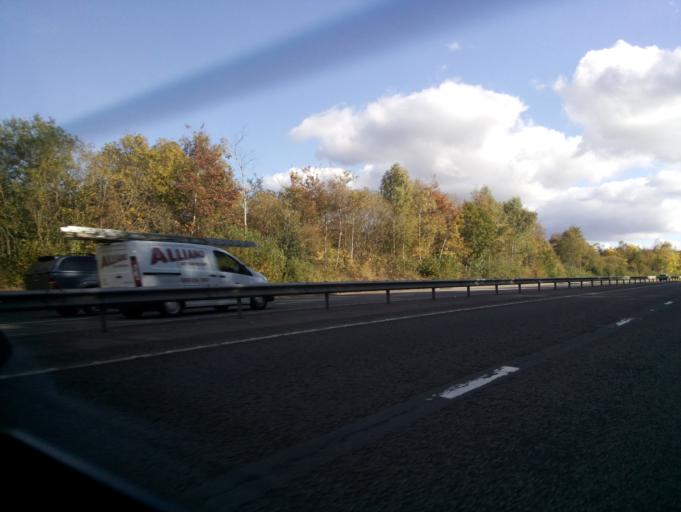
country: GB
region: Wales
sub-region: Merthyr Tydfil County Borough
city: Abercanaid
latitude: 51.7233
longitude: -3.3704
